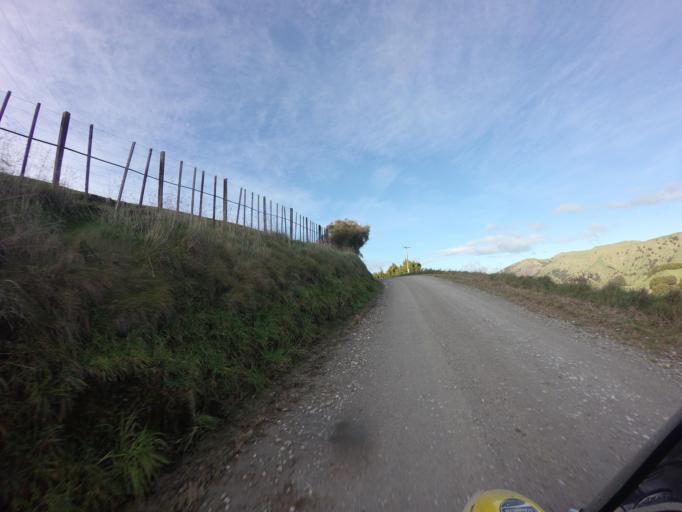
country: NZ
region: Hawke's Bay
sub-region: Wairoa District
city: Wairoa
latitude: -38.7190
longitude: 177.5471
